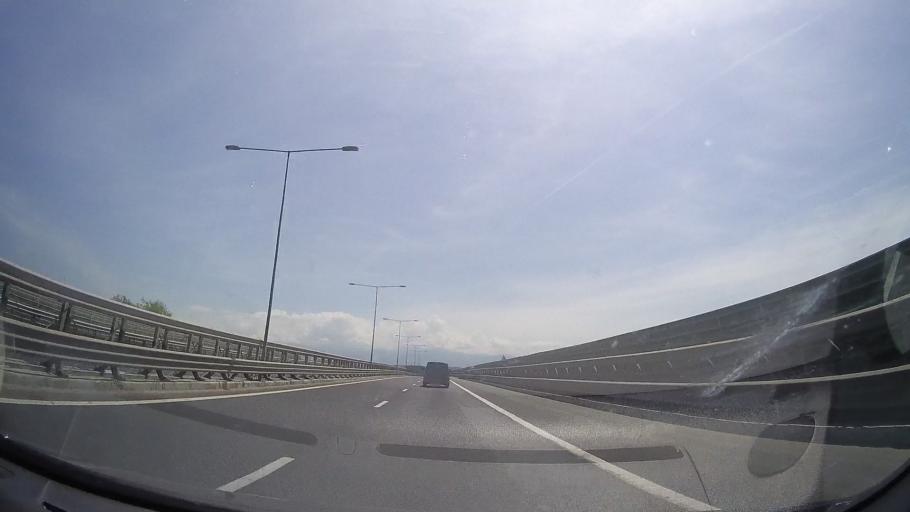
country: RO
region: Sibiu
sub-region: Municipiul Sibiu
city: Sibiu
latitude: 45.8090
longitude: 24.1737
